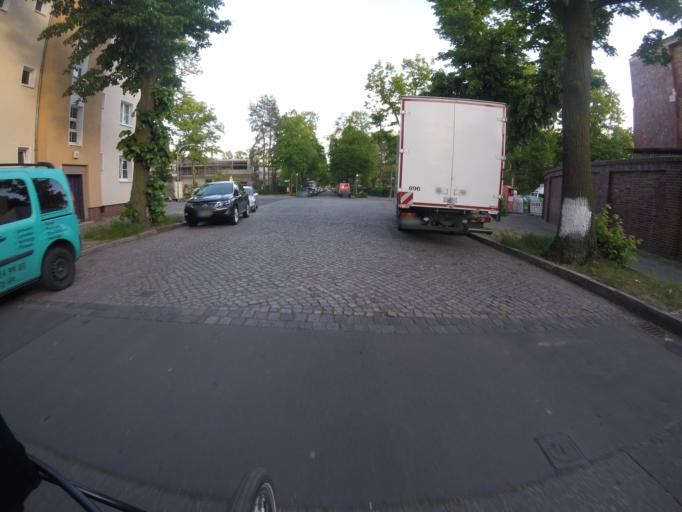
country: DE
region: Berlin
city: Tegel
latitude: 52.5790
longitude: 13.2838
